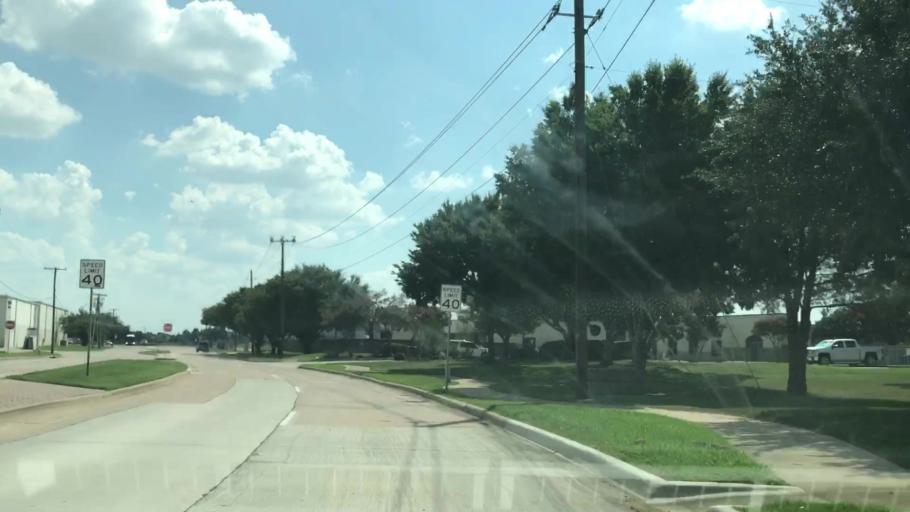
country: US
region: Texas
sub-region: Dallas County
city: Carrollton
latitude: 32.9490
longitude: -96.9167
